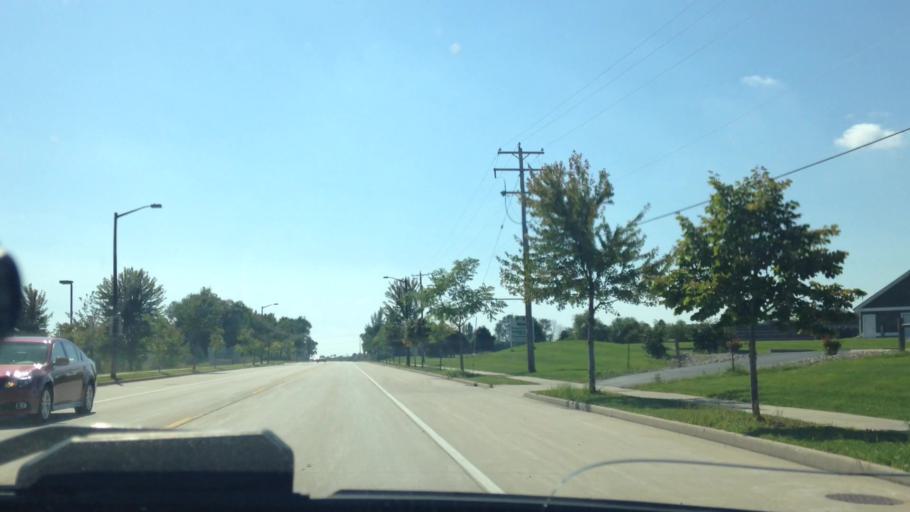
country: US
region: Wisconsin
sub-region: Ozaukee County
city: Port Washington
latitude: 43.3750
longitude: -87.8947
